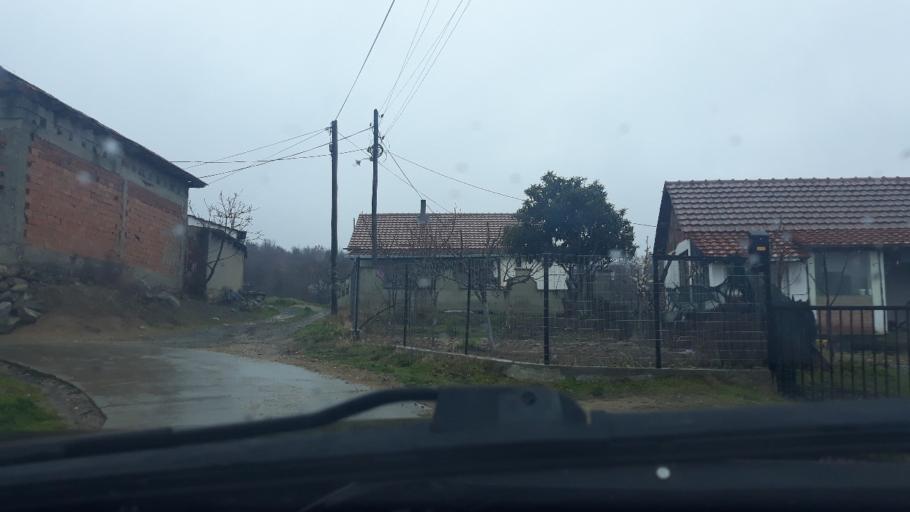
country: MK
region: Bogdanci
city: Bogdanci
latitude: 41.2392
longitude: 22.6122
